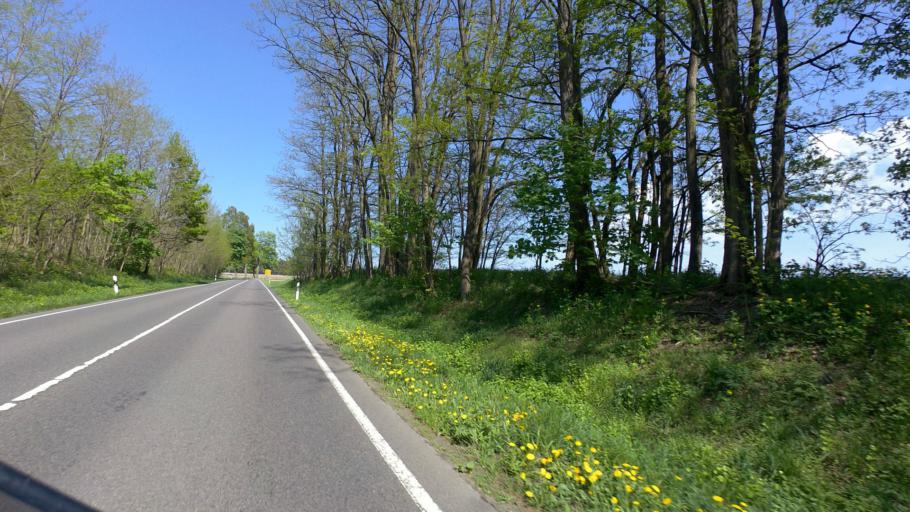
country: DE
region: Brandenburg
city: Lieberose
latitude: 52.0000
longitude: 14.3091
